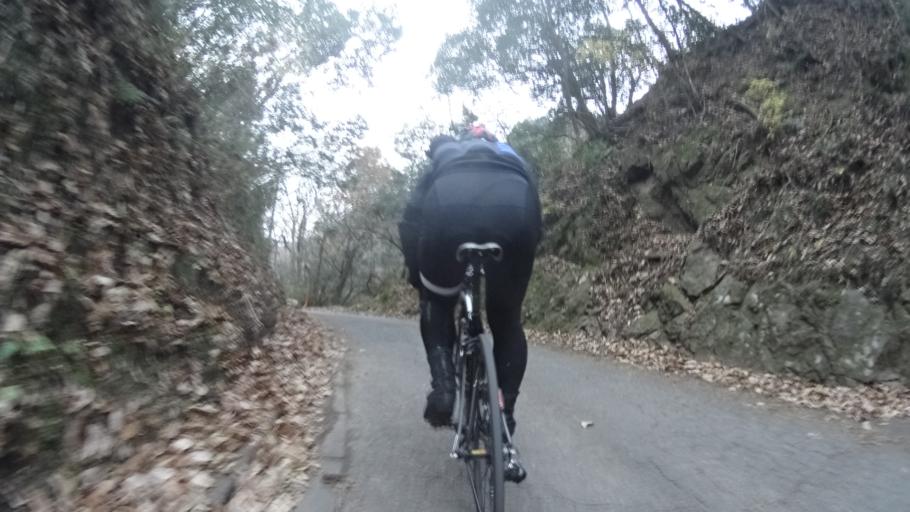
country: JP
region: Yamanashi
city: Uenohara
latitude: 35.6202
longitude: 139.1580
